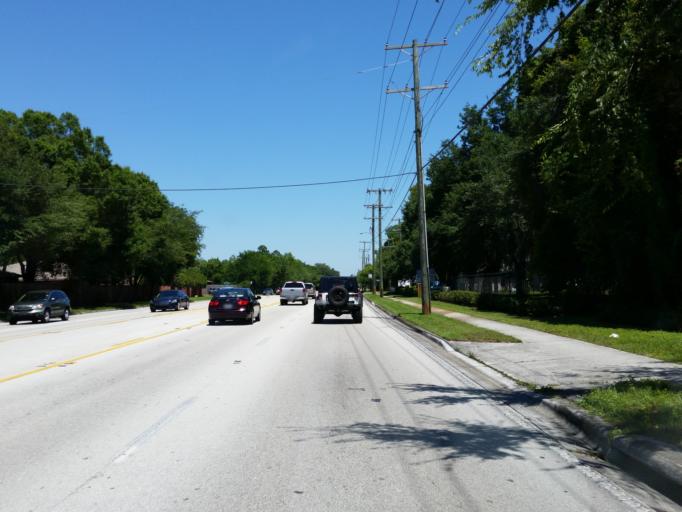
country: US
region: Florida
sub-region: Hillsborough County
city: Bloomingdale
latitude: 27.8936
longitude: -82.2834
